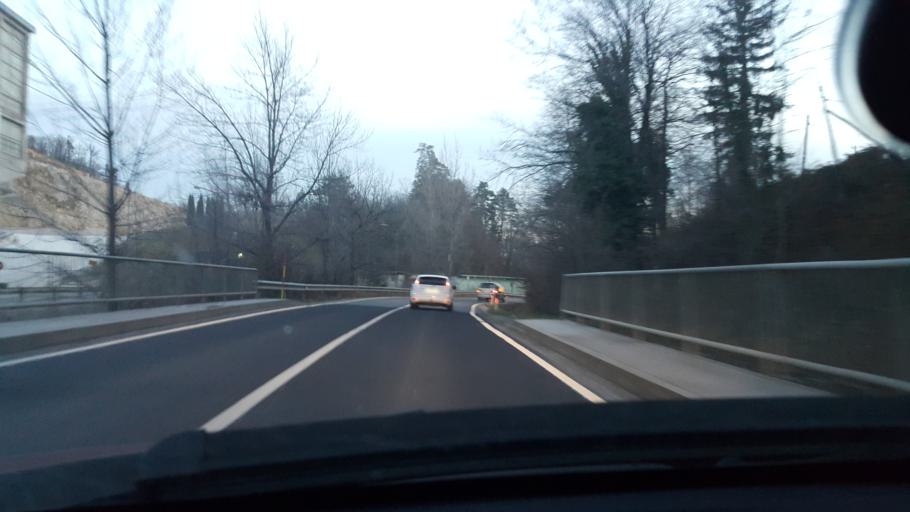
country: SI
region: Zalec
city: Gotovlje
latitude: 46.2915
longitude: 15.1731
